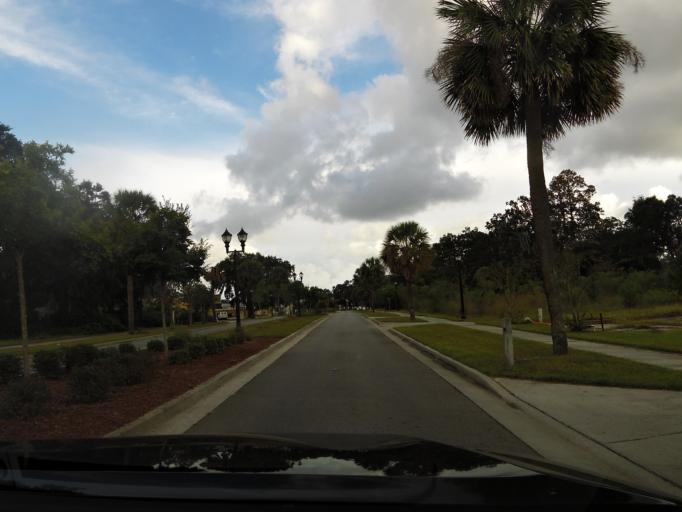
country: US
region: Georgia
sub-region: Liberty County
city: Hinesville
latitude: 31.8529
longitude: -81.6015
